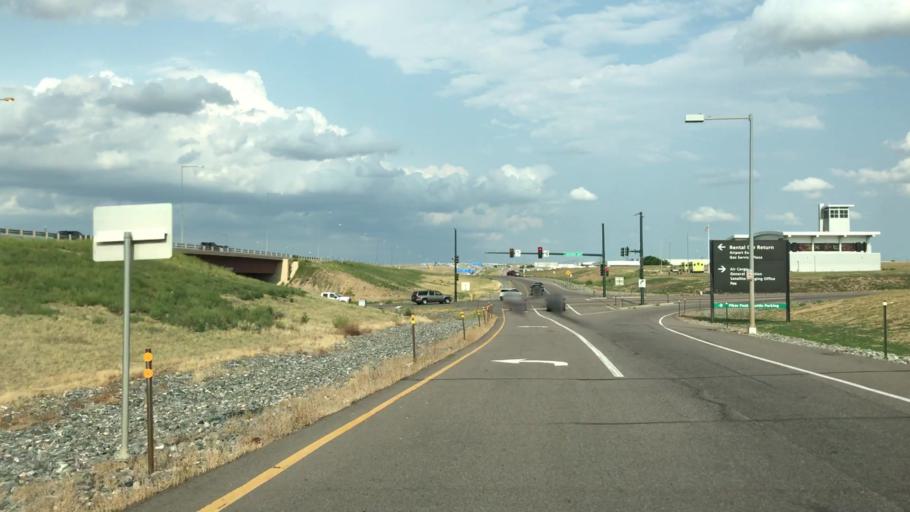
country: US
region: Colorado
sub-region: Adams County
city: Aurora
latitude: 39.8331
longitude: -104.6943
